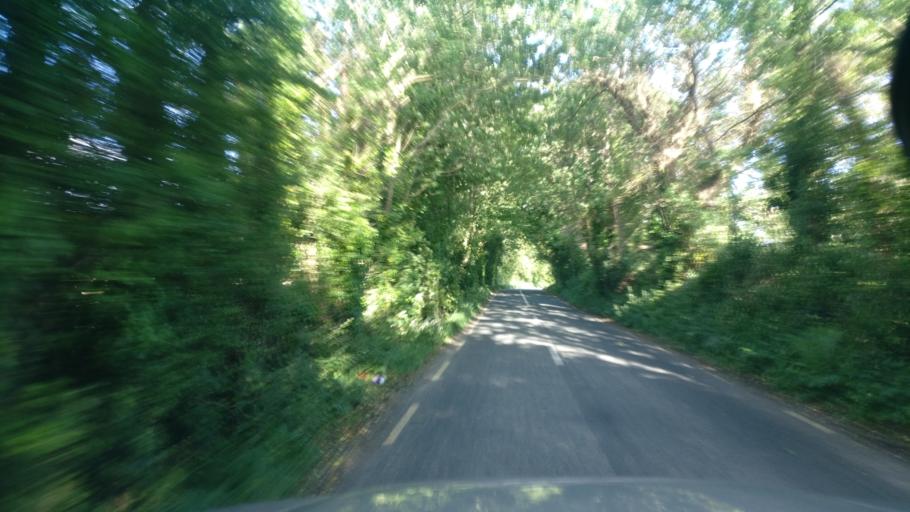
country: IE
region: Connaught
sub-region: County Galway
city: Ballinasloe
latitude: 53.2232
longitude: -8.1996
